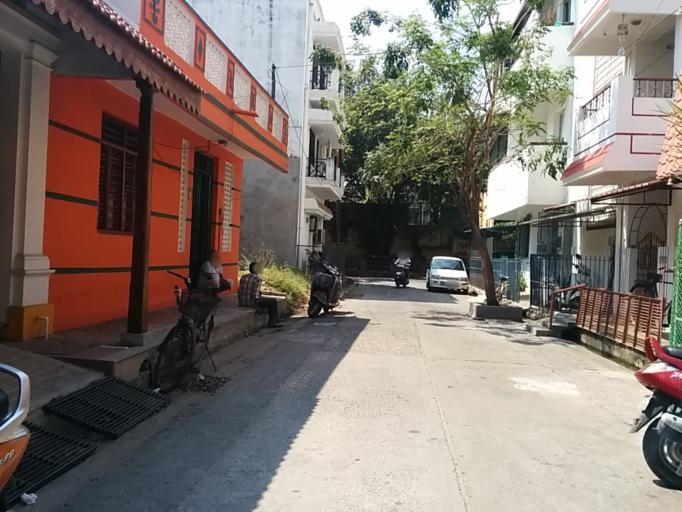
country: IN
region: Pondicherry
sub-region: Puducherry
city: Puducherry
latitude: 11.9389
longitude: 79.8323
